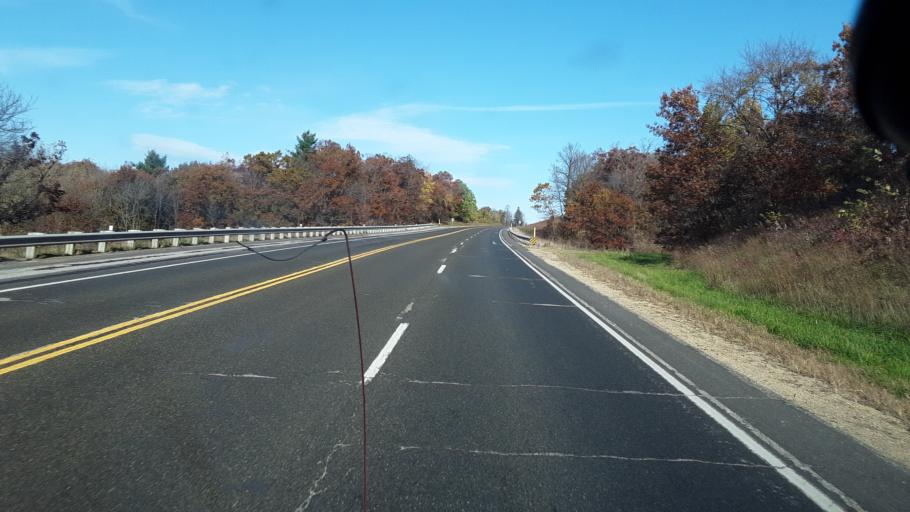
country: US
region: Wisconsin
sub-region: Monroe County
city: Tomah
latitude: 43.8923
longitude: -90.4859
